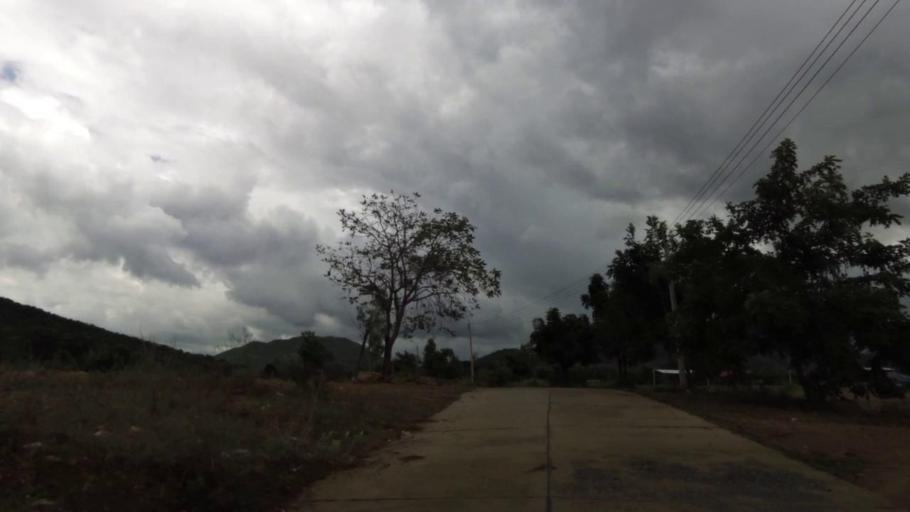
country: TH
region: Nakhon Sawan
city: Phai Sali
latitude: 15.6036
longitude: 100.6759
